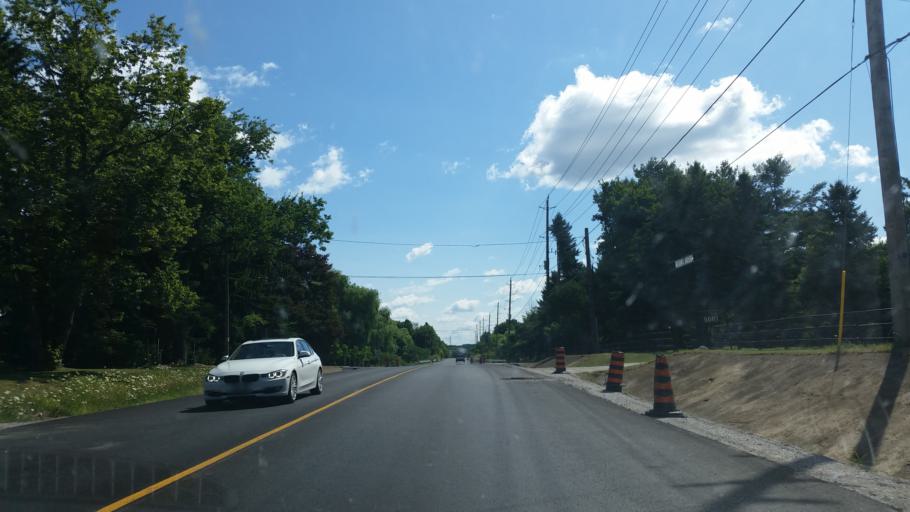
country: CA
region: Ontario
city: Vaughan
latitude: 43.9042
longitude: -79.6402
